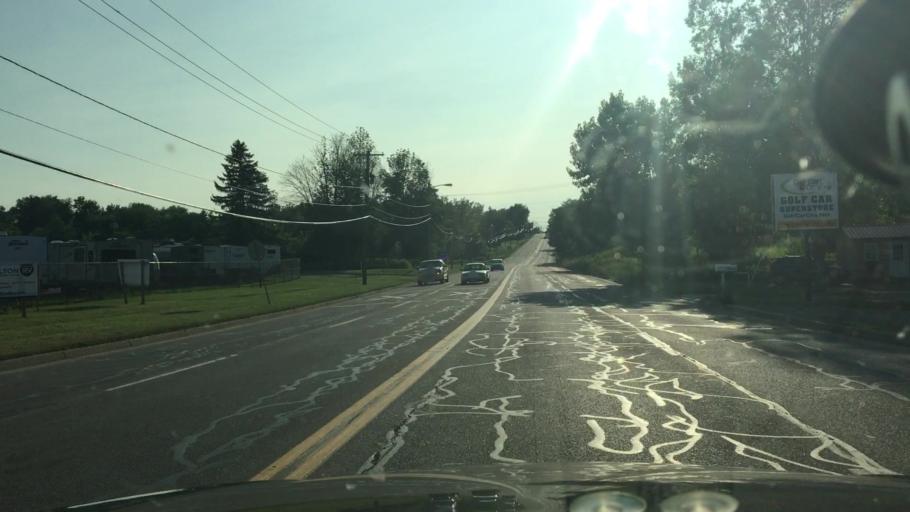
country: US
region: New York
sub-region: Erie County
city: Blasdell
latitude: 42.7968
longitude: -78.8008
